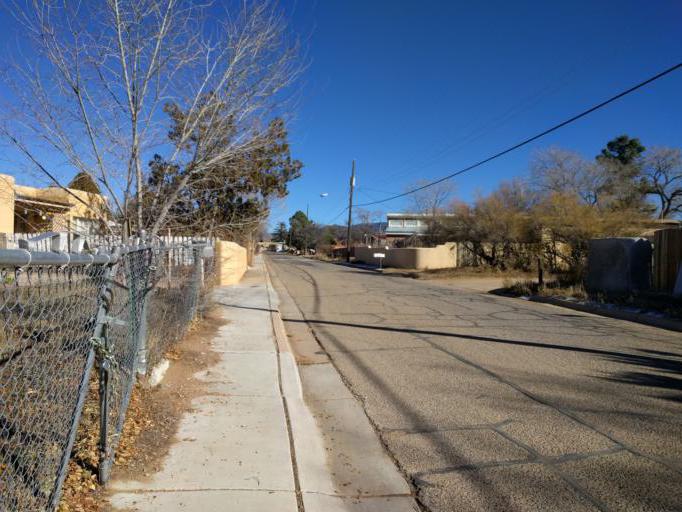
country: US
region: New Mexico
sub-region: Santa Fe County
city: Santa Fe
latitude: 35.6661
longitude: -105.9653
